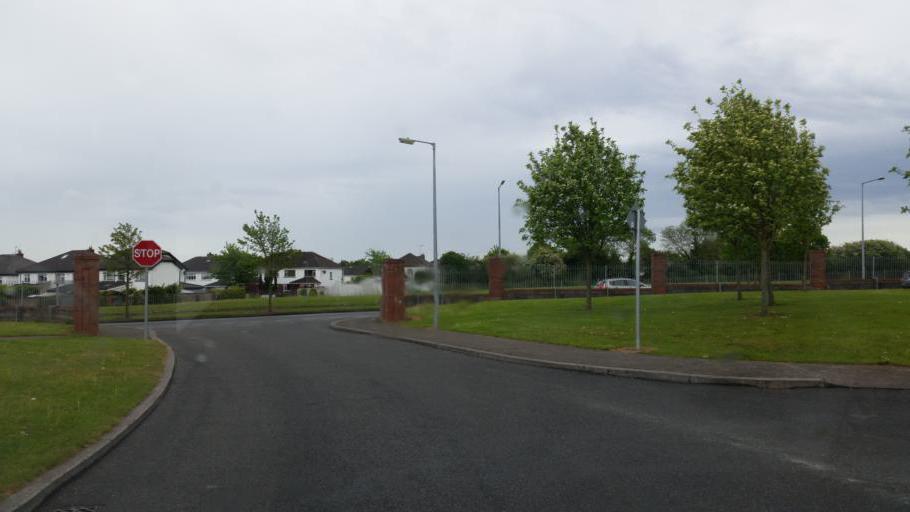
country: IE
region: Leinster
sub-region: Fingal County
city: Swords
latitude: 53.4636
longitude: -6.2401
